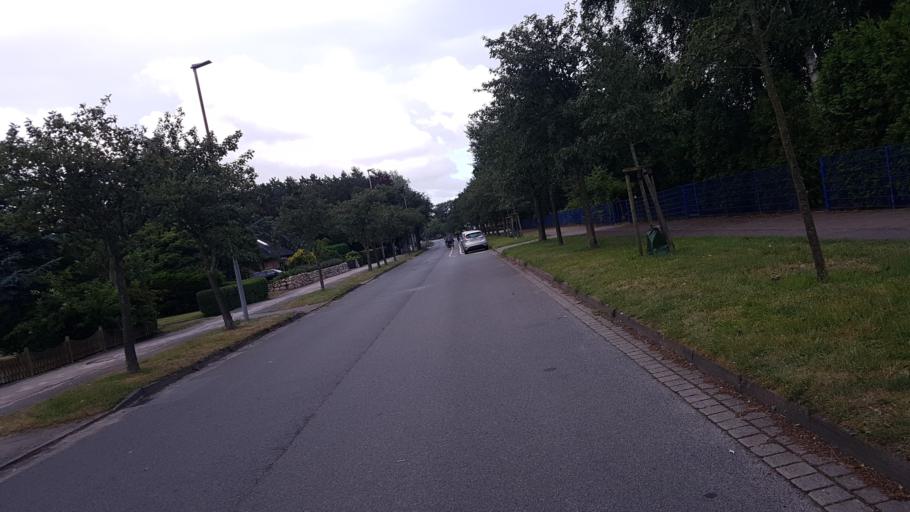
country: DE
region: Schleswig-Holstein
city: Sankt Peter-Ording
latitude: 54.2957
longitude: 8.6474
